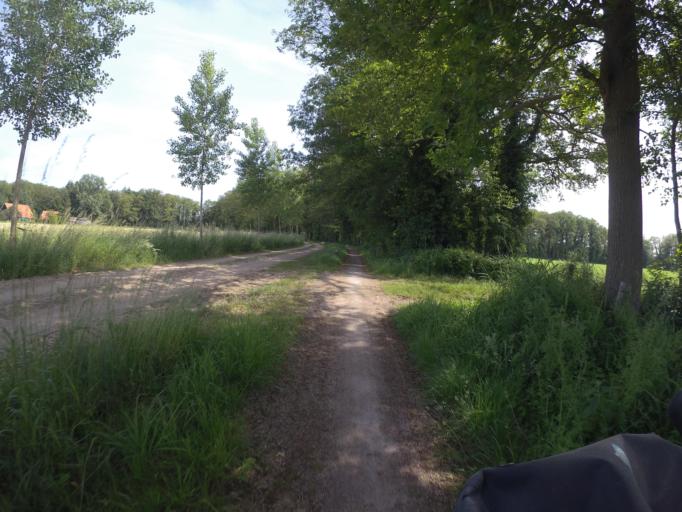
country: NL
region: Gelderland
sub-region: Gemeente Aalten
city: Bredevoort
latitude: 51.9409
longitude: 6.6575
